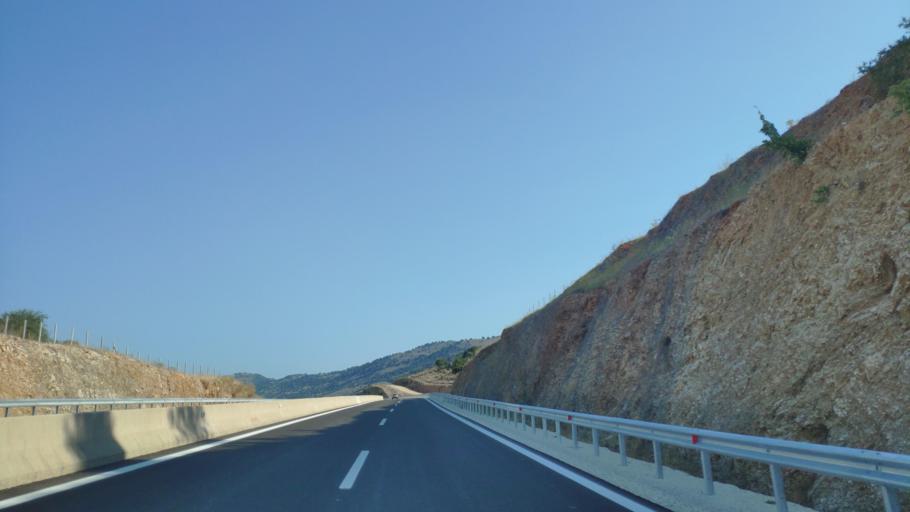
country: GR
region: West Greece
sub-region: Nomos Aitolias kai Akarnanias
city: Katouna
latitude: 38.8045
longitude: 21.1316
